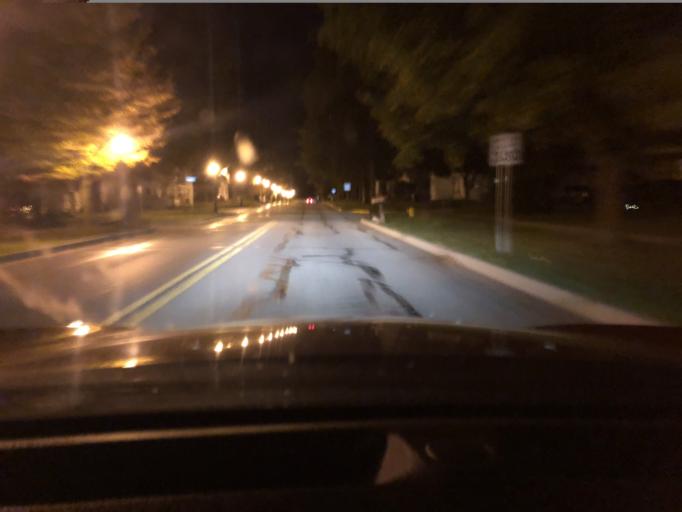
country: US
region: Indiana
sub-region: DeKalb County
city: Waterloo
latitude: 41.4296
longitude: -85.0200
